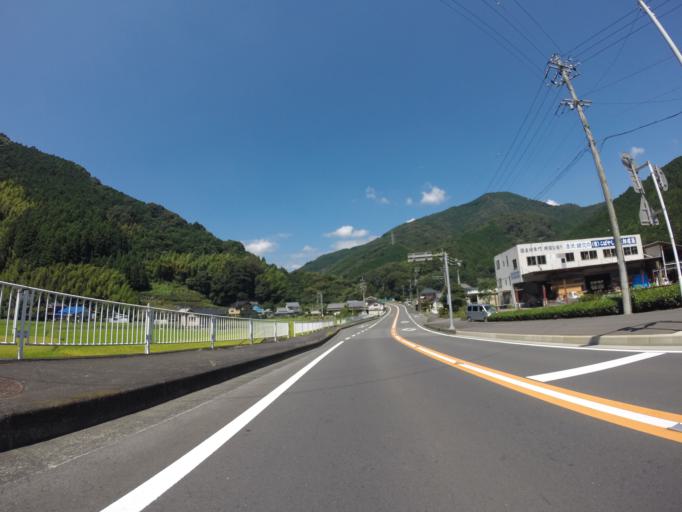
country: JP
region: Shizuoka
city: Shizuoka-shi
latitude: 35.0159
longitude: 138.2685
